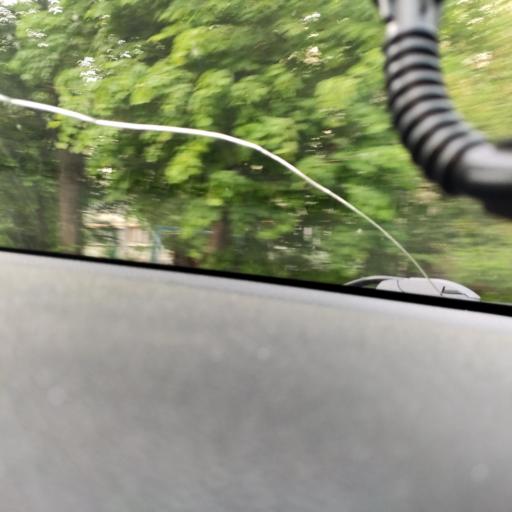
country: RU
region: Tatarstan
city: Osinovo
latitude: 55.8456
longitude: 48.9018
